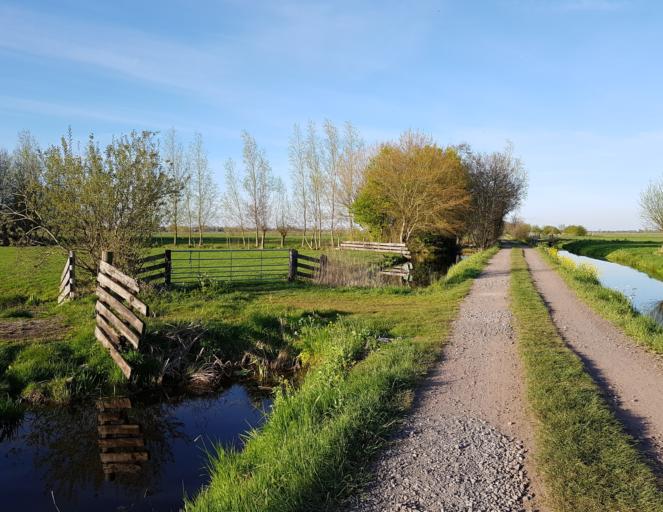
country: NL
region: South Holland
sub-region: Gemeente Gouda
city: Gouda
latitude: 51.9561
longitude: 4.6955
